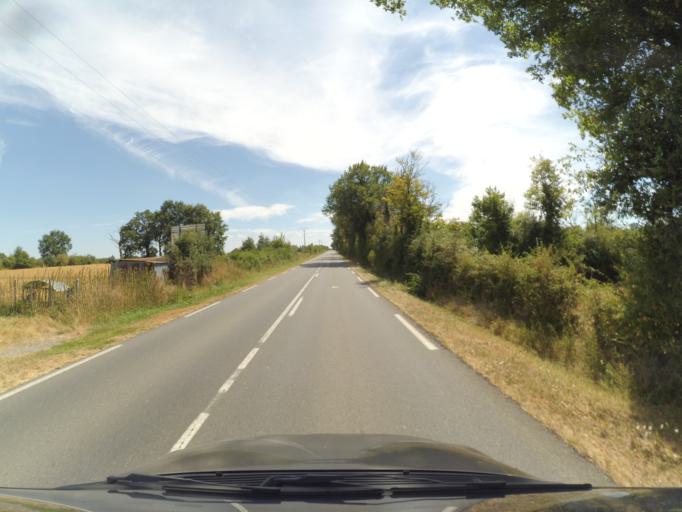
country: FR
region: Poitou-Charentes
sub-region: Departement de la Vienne
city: Availles-Limouzine
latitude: 46.1012
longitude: 0.5806
